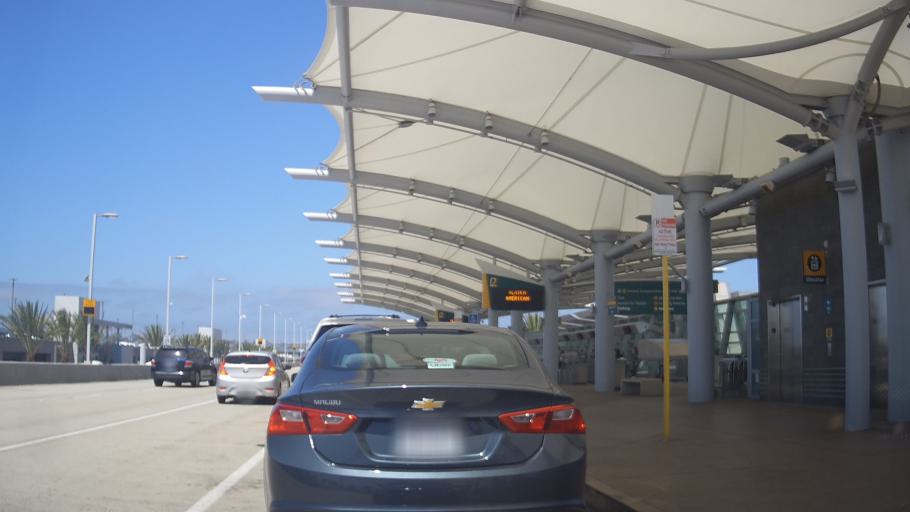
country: US
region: California
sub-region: San Diego County
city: San Diego
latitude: 32.7306
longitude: -117.1997
